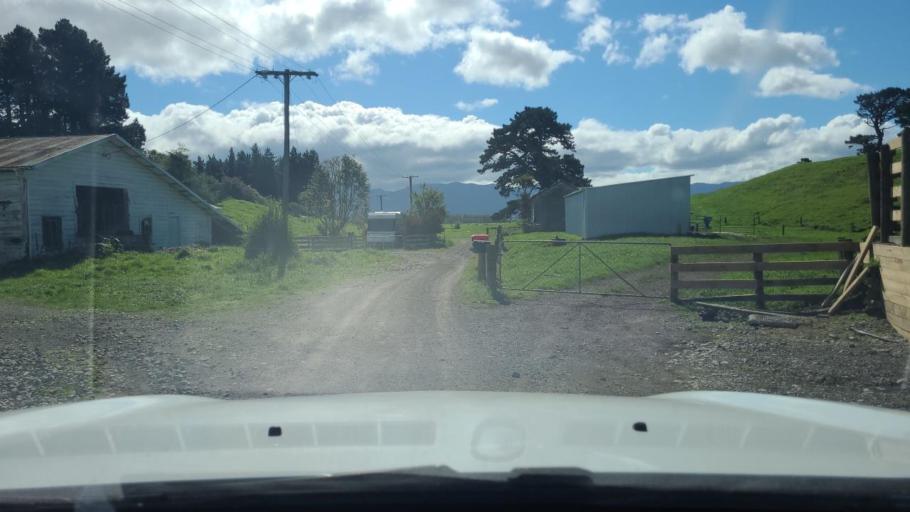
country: NZ
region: Wellington
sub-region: Upper Hutt City
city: Upper Hutt
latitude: -41.2216
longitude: 175.3072
